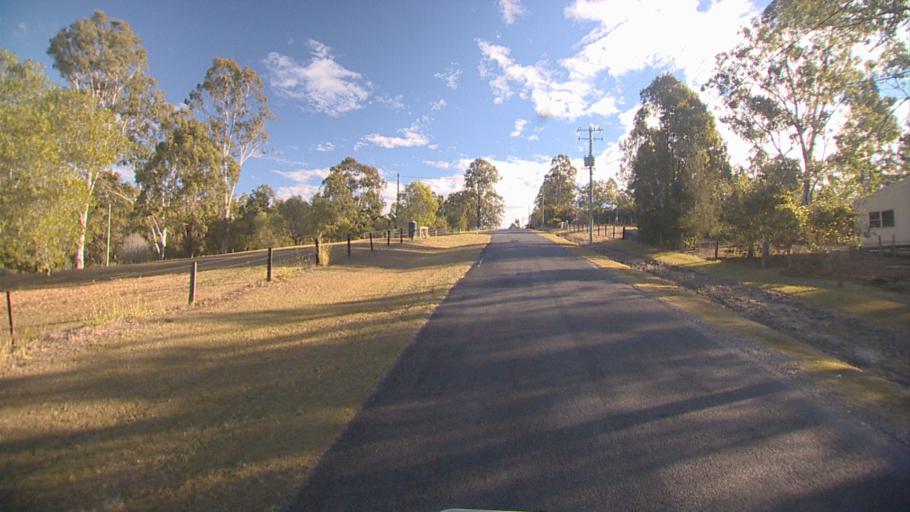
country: AU
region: Queensland
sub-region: Logan
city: Cedar Vale
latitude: -27.9302
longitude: 153.0658
